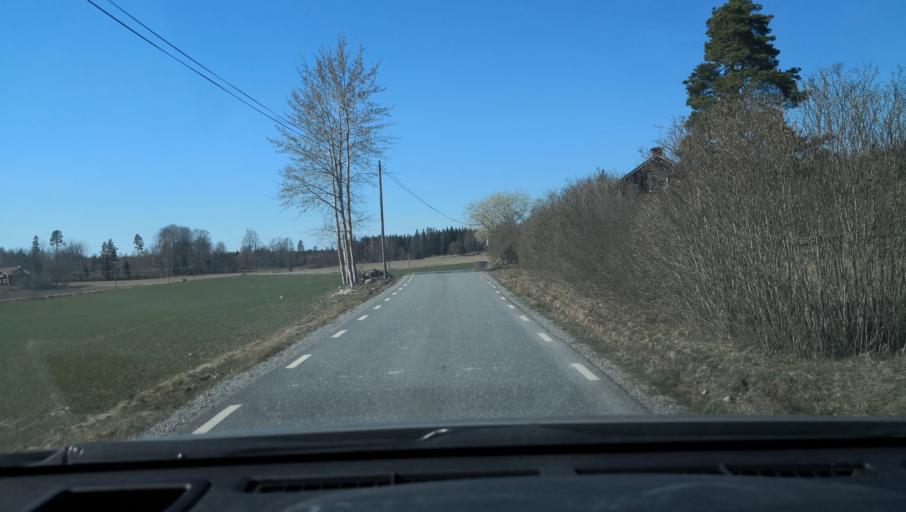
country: SE
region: Vaestmanland
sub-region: Sala Kommun
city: Sala
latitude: 59.9281
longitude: 16.4650
